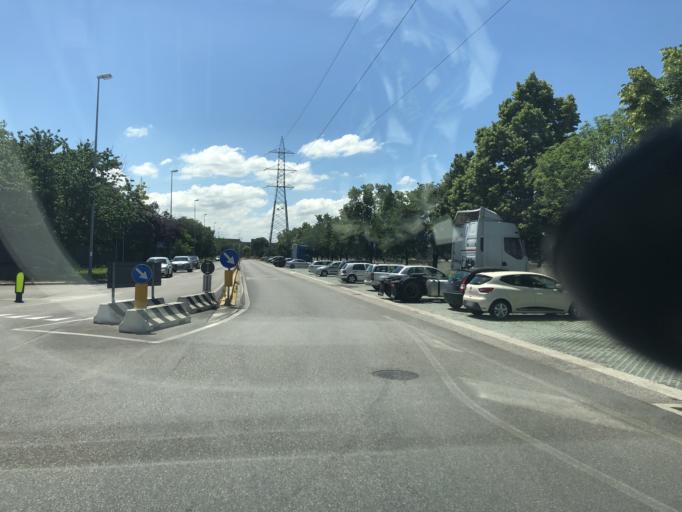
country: IT
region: Veneto
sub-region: Provincia di Verona
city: Dossobuono
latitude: 45.4219
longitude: 10.9318
